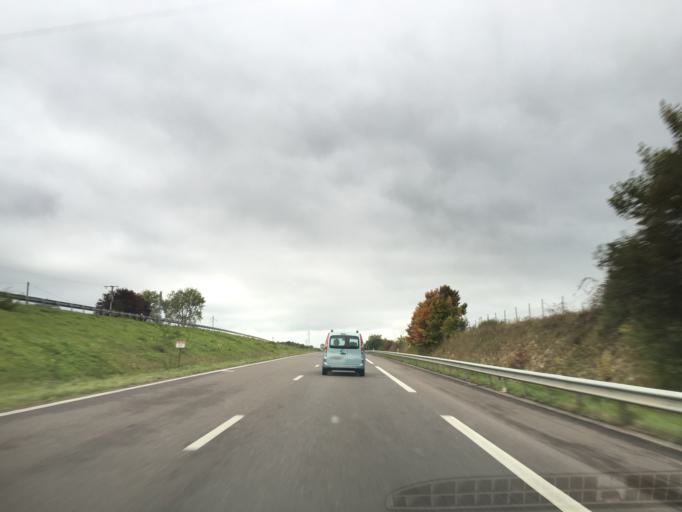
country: FR
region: Lorraine
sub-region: Departement de la Meuse
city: Euville
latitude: 48.6901
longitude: 5.6862
